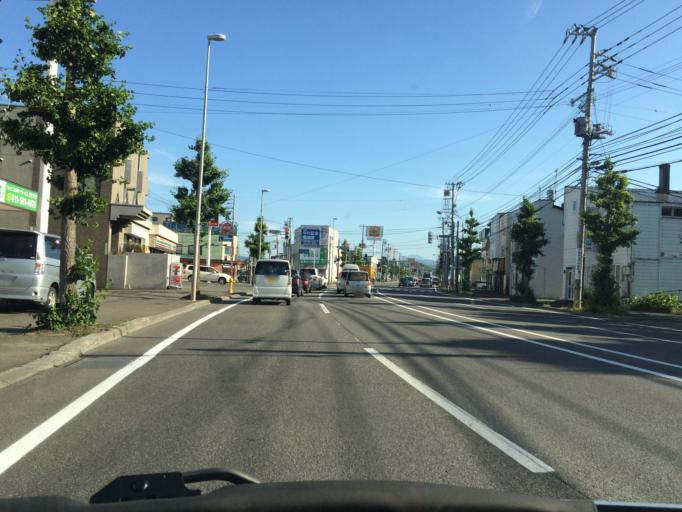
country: JP
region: Hokkaido
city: Sapporo
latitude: 43.0156
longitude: 141.3468
